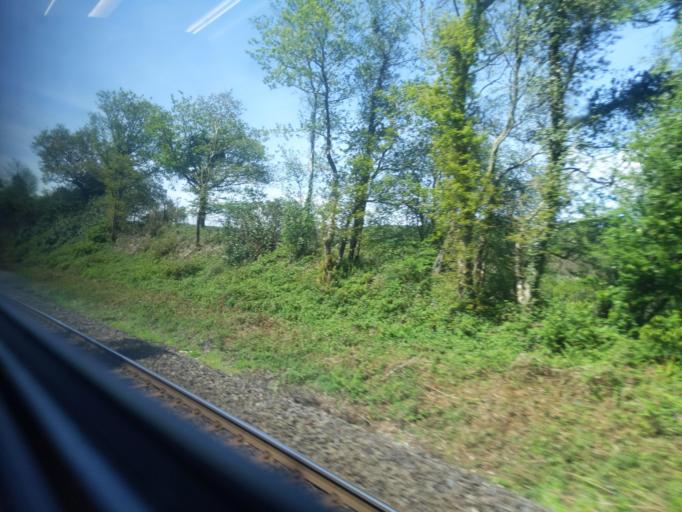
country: GB
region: England
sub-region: Cornwall
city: Lostwithiel
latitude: 50.4567
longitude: -4.5999
